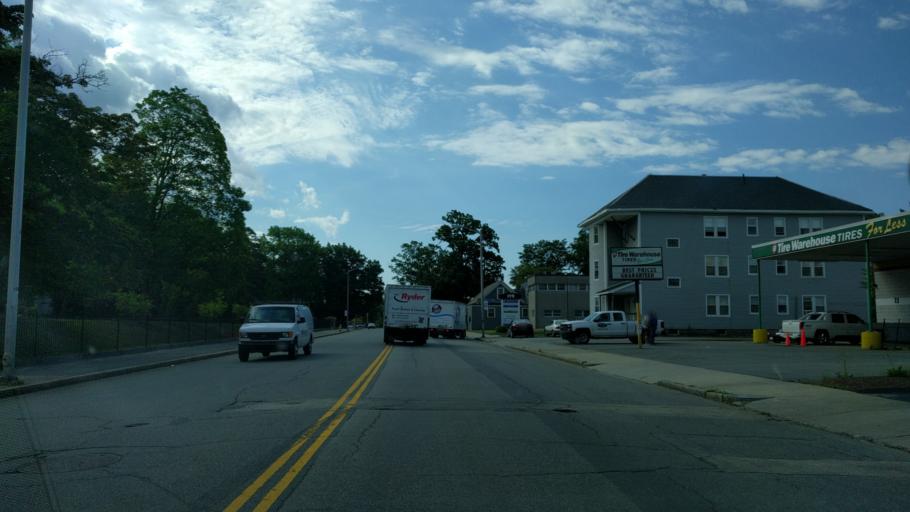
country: US
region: Massachusetts
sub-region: Worcester County
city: Worcester
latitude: 42.2802
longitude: -71.8050
